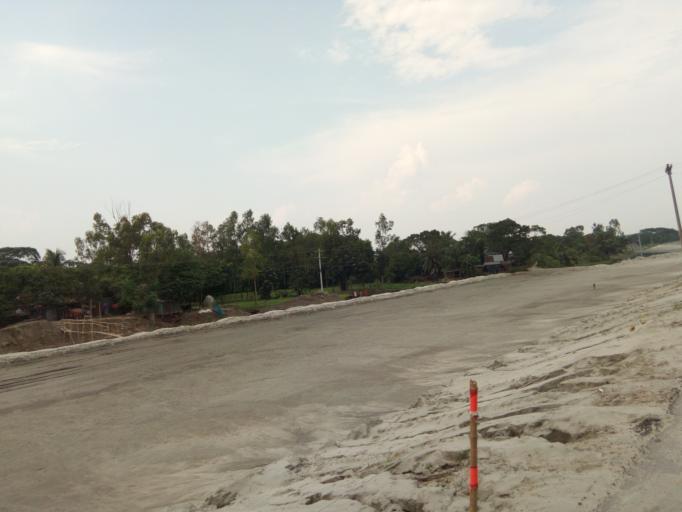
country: BD
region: Dhaka
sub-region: Dhaka
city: Dhaka
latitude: 23.6112
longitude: 90.3285
